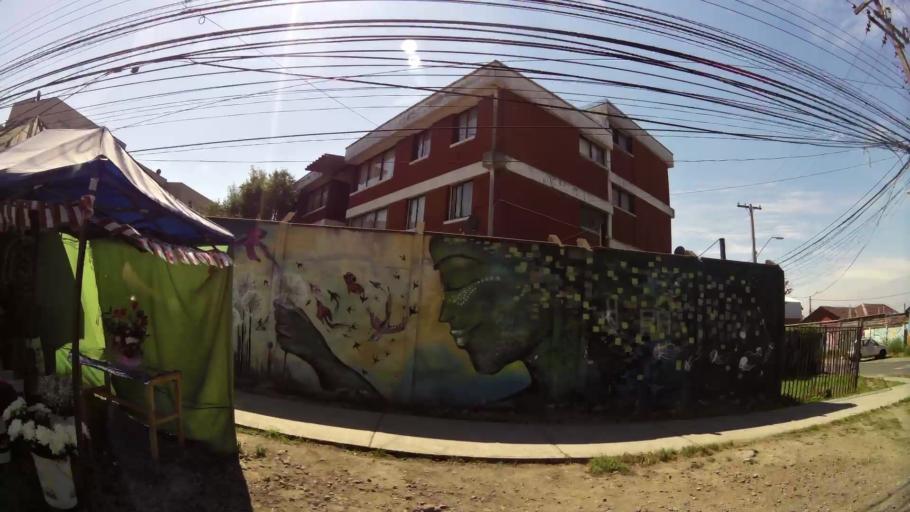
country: CL
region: Santiago Metropolitan
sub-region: Provincia de Santiago
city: La Pintana
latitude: -33.5277
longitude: -70.6540
